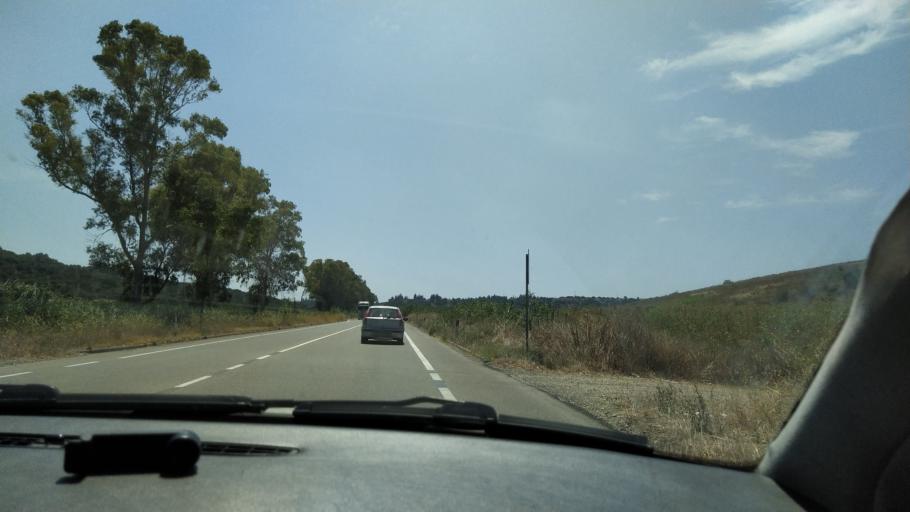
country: IT
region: Apulia
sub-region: Provincia di Taranto
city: Marina di Ginosa
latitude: 40.4399
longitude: 16.7842
